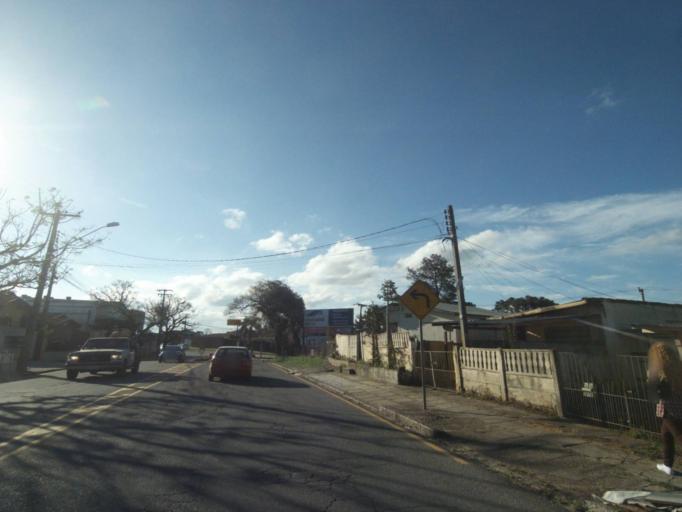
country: BR
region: Parana
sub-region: Curitiba
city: Curitiba
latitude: -25.3908
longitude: -49.2571
